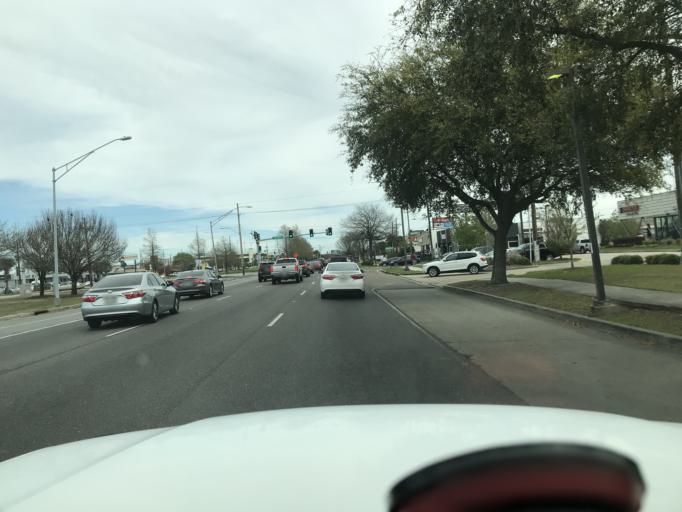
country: US
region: Louisiana
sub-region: Jefferson Parish
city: Metairie
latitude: 30.0035
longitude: -90.1630
